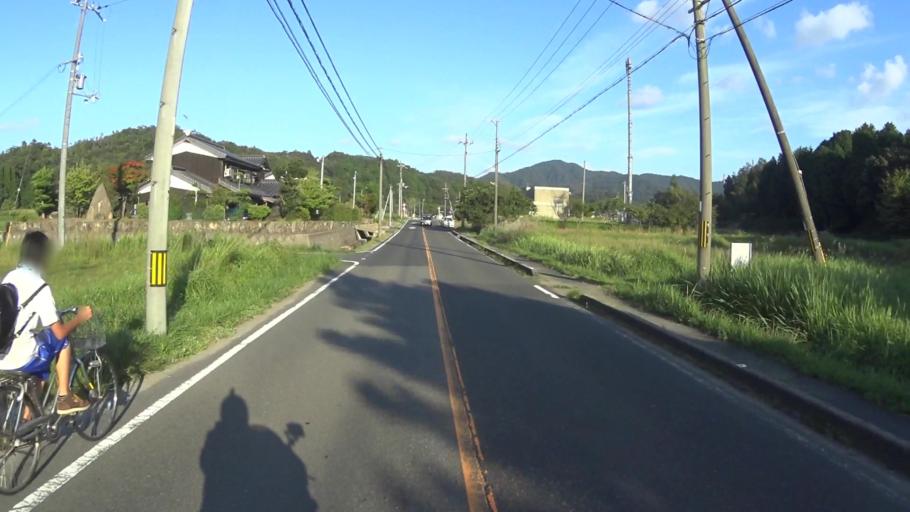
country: JP
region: Hyogo
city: Toyooka
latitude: 35.5805
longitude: 134.9667
